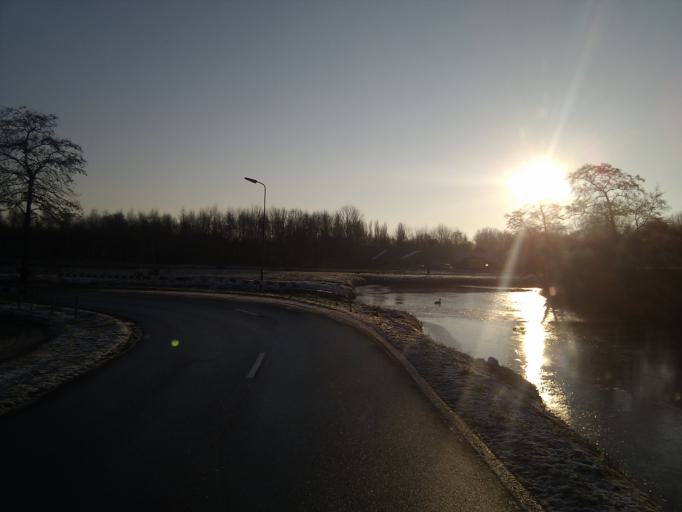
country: NL
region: Utrecht
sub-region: Gemeente Utrecht
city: Utrecht
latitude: 52.1301
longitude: 5.1028
